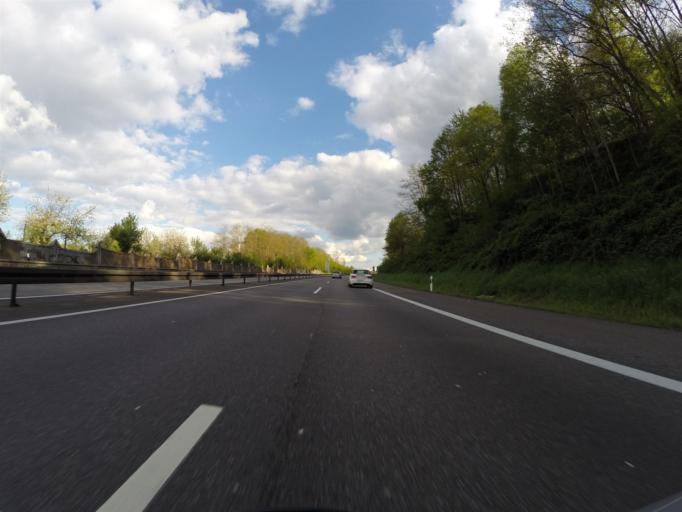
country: DE
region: Saarland
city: Saarlouis
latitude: 49.2974
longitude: 6.7520
